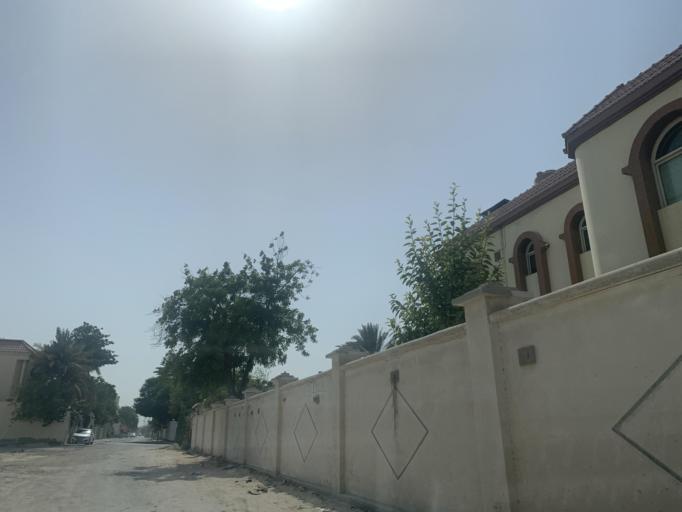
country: BH
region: Northern
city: Madinat `Isa
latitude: 26.1954
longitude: 50.5025
